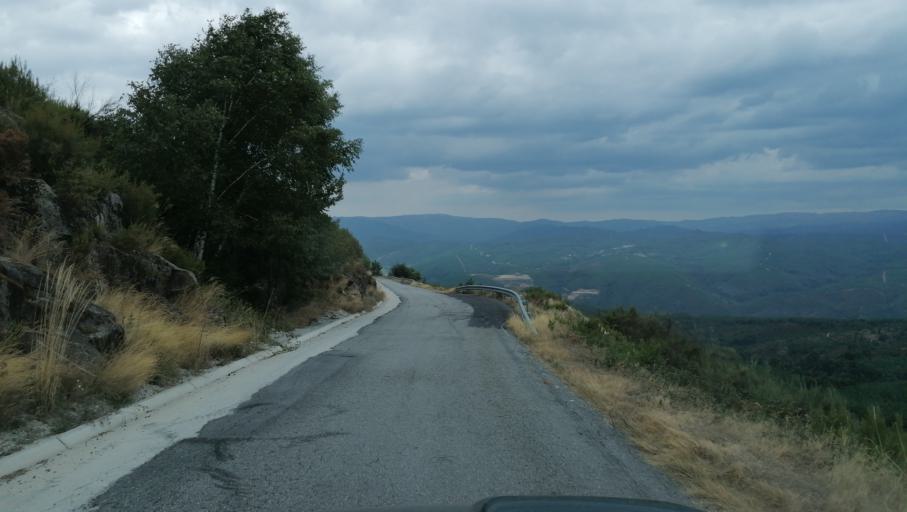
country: PT
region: Vila Real
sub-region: Vila Pouca de Aguiar
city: Vila Pouca de Aguiar
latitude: 41.5593
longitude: -7.6952
